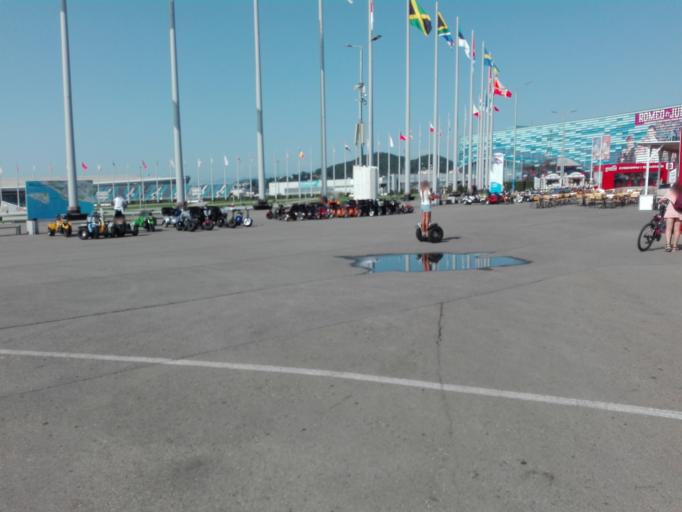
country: RU
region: Krasnodarskiy
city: Adler
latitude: 43.4046
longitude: 39.9562
